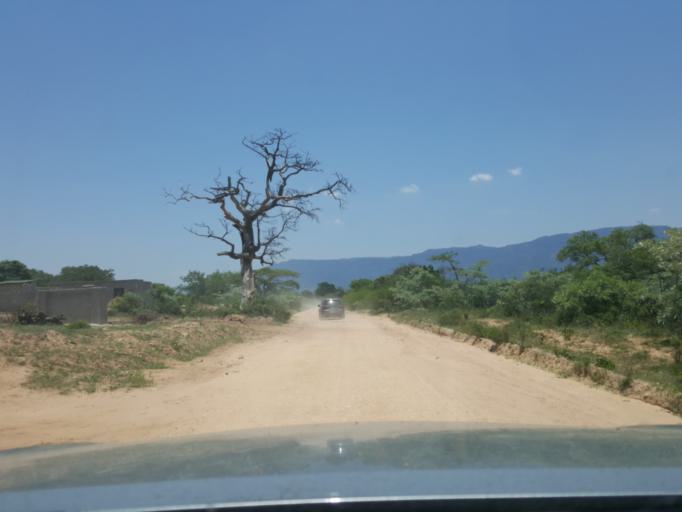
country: ZA
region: Limpopo
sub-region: Mopani District Municipality
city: Hoedspruit
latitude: -24.5809
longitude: 30.9903
